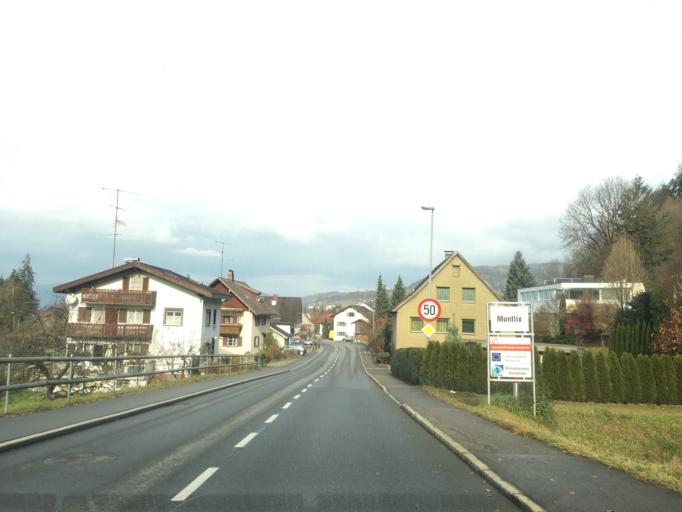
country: AT
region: Vorarlberg
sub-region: Politischer Bezirk Feldkirch
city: Sulz
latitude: 47.2759
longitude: 9.6596
